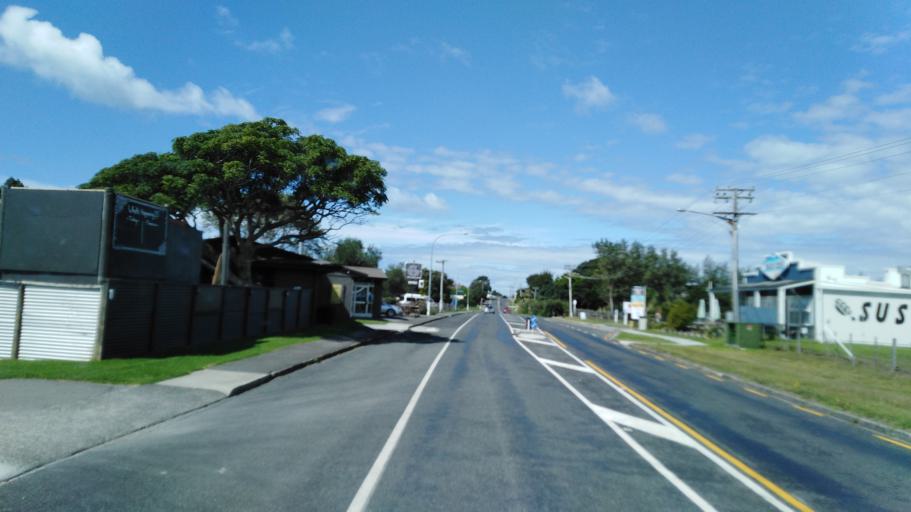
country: NZ
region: Bay of Plenty
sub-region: Western Bay of Plenty District
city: Waihi Beach
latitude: -37.4090
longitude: 175.9376
